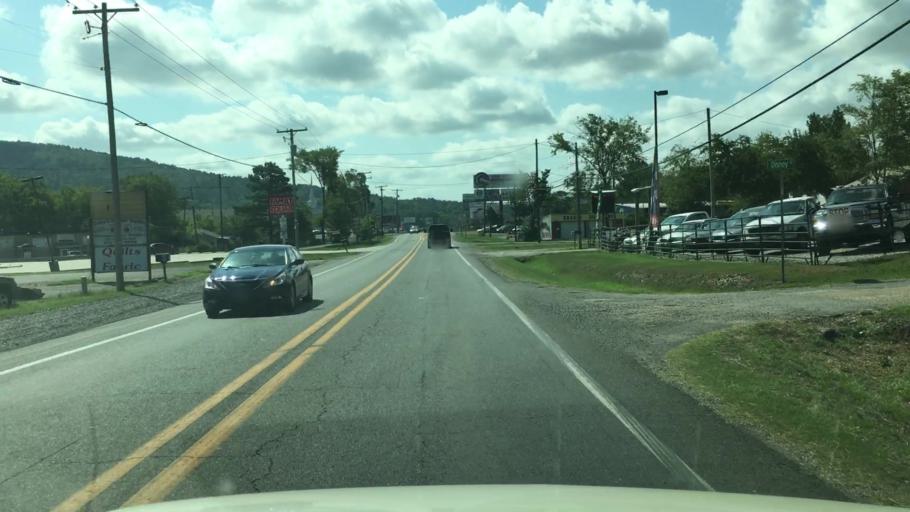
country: US
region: Arkansas
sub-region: Garland County
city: Piney
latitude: 34.5067
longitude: -93.1301
